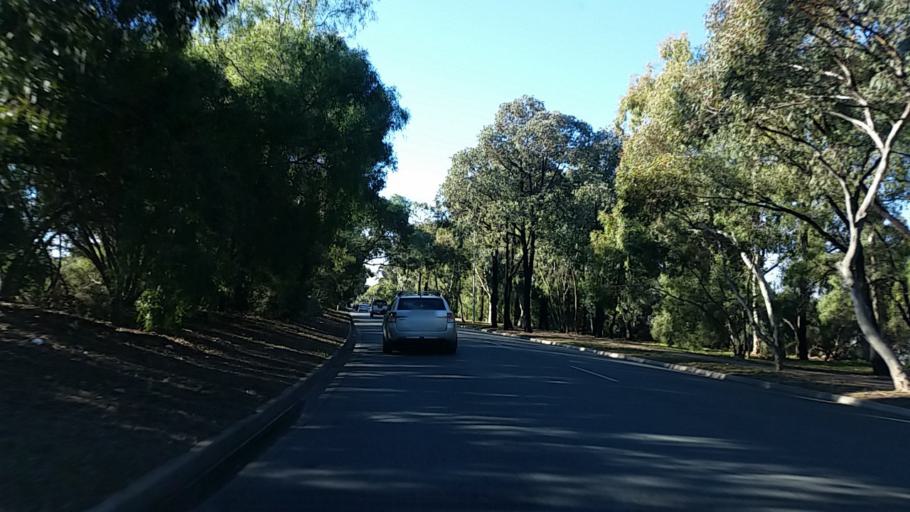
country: AU
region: South Australia
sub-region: Salisbury
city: Salisbury
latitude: -34.7805
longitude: 138.6095
